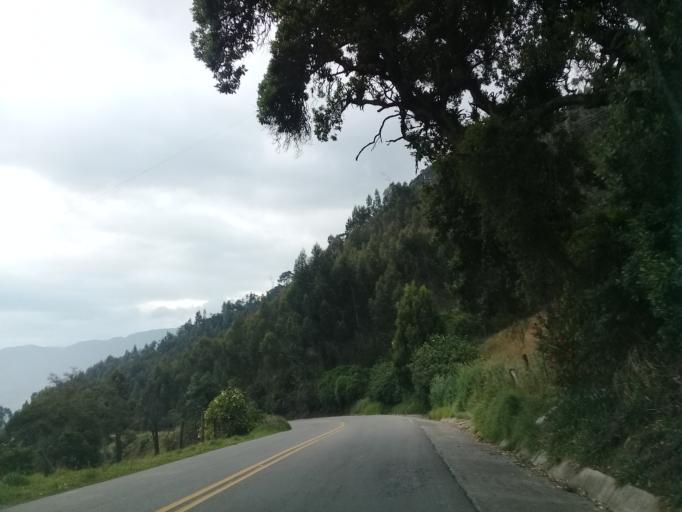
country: CO
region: Cundinamarca
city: Zipaquira
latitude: 5.0308
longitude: -74.0293
